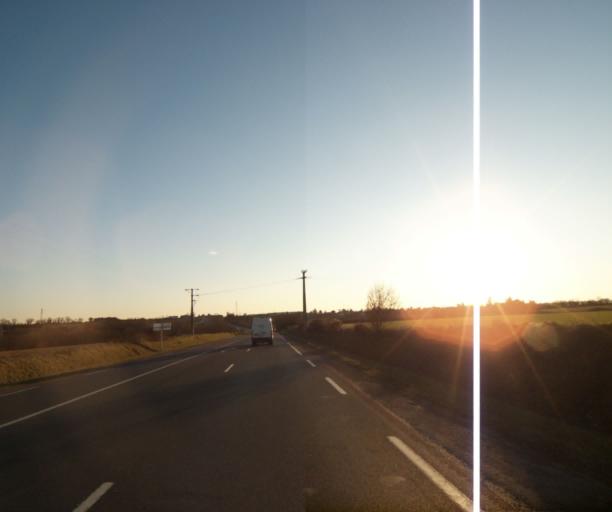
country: FR
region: Poitou-Charentes
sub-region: Departement des Deux-Sevres
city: Echire
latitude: 46.3582
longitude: -0.4353
